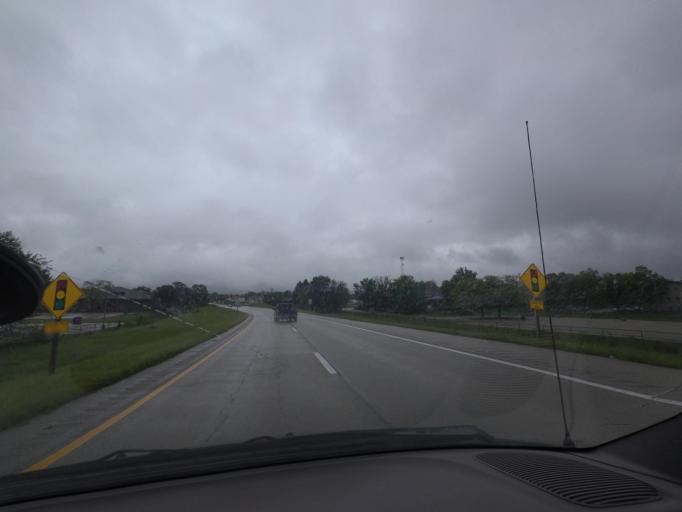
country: US
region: Illinois
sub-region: Champaign County
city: Champaign
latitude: 40.1168
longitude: -88.2845
